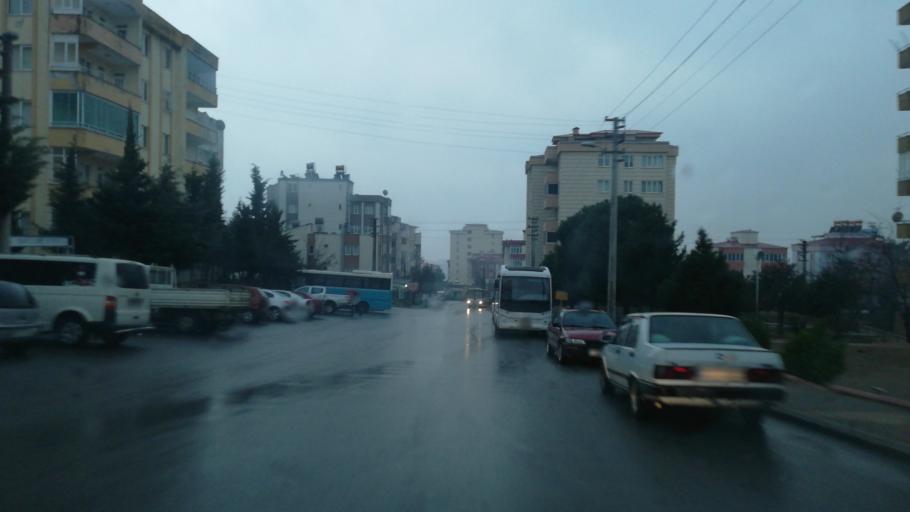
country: TR
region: Kahramanmaras
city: Kahramanmaras
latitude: 37.5957
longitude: 36.8993
